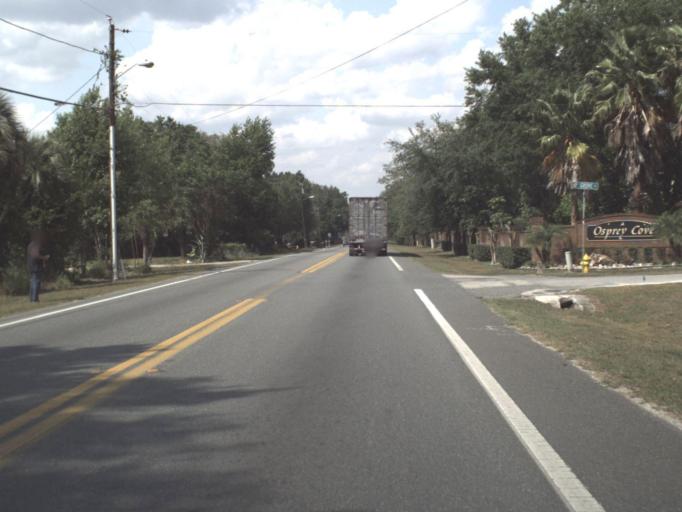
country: US
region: Florida
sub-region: Lake County
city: Groveland
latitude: 28.5651
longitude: -81.8555
